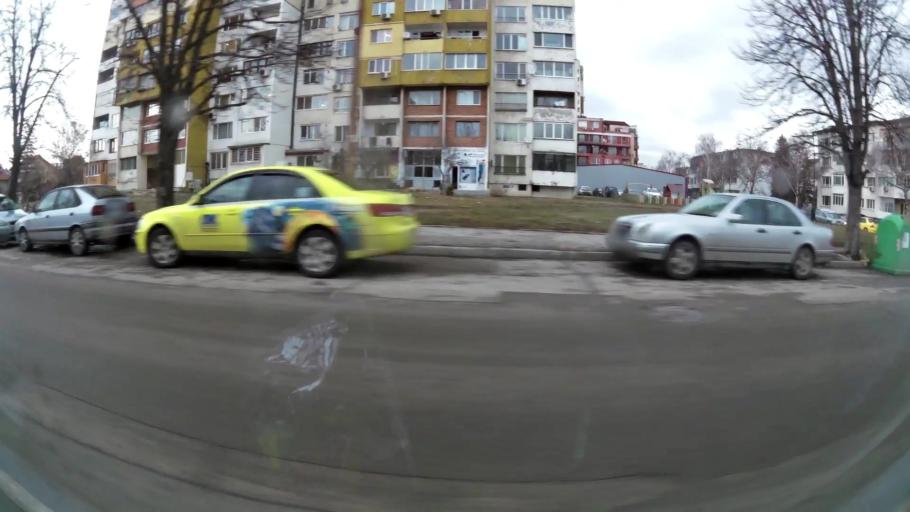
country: BG
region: Sofia-Capital
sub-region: Stolichna Obshtina
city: Sofia
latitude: 42.7332
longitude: 23.2982
